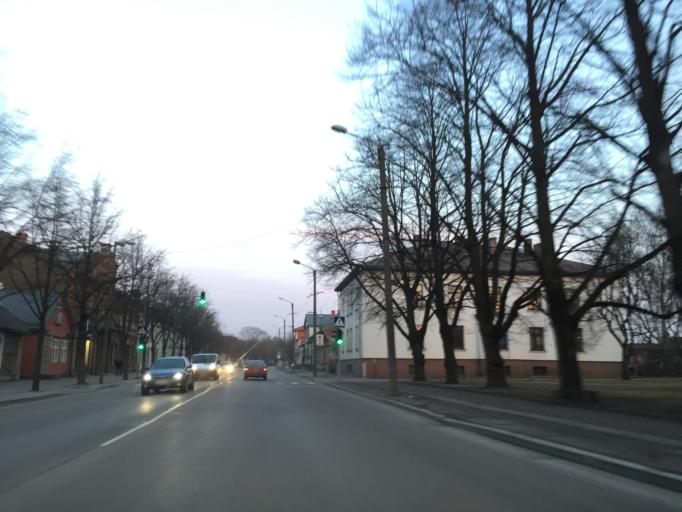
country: EE
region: Paernumaa
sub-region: Paernu linn
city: Parnu
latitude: 58.3827
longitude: 24.5183
